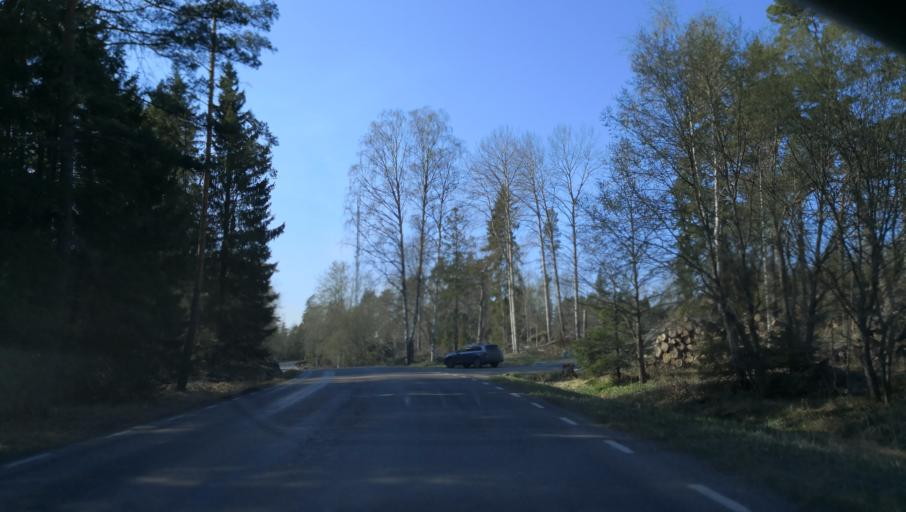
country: SE
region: Stockholm
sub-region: Varmdo Kommun
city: Hemmesta
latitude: 59.3140
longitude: 18.5752
